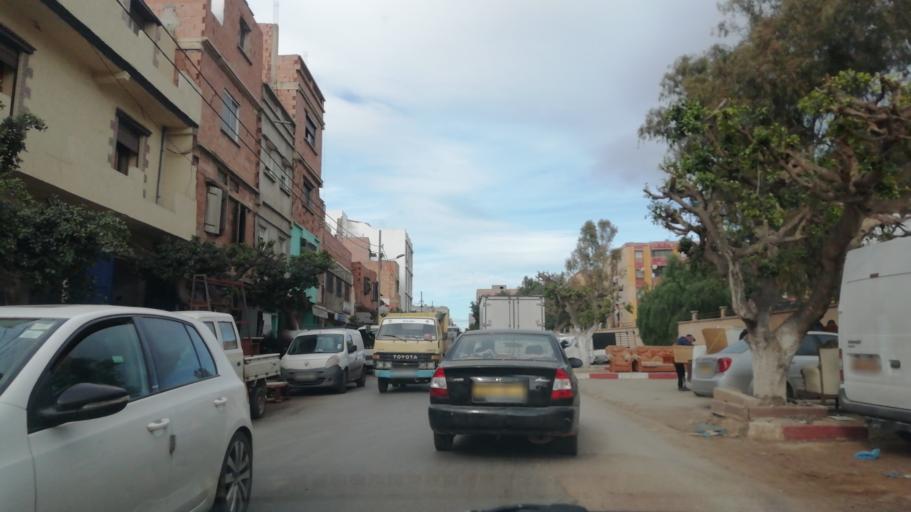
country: DZ
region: Oran
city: Oran
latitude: 35.6834
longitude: -0.6132
